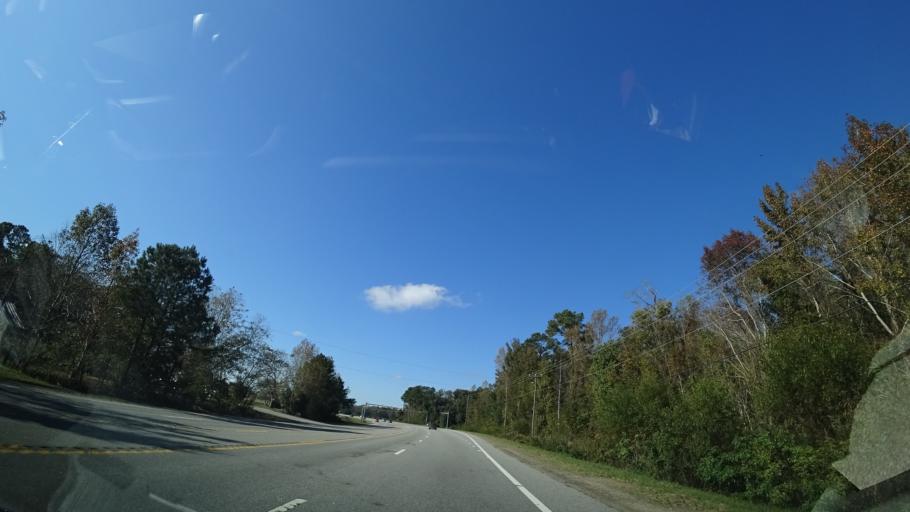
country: US
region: North Carolina
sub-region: Currituck County
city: Currituck
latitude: 36.4545
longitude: -76.0273
